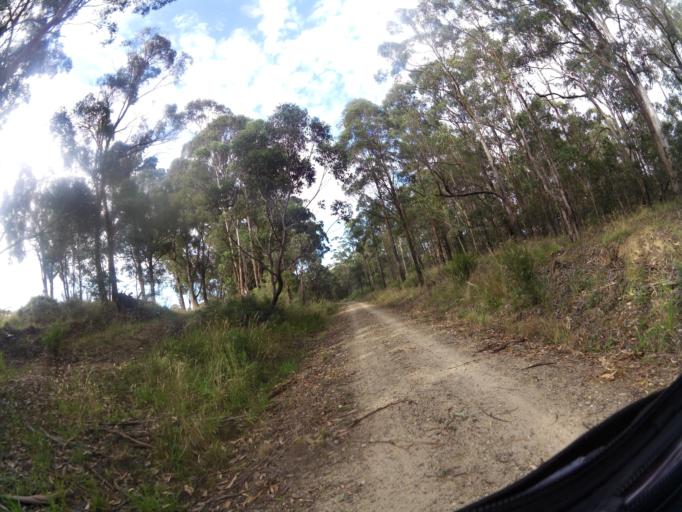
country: AU
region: Victoria
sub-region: East Gippsland
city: Lakes Entrance
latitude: -37.7368
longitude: 148.4219
